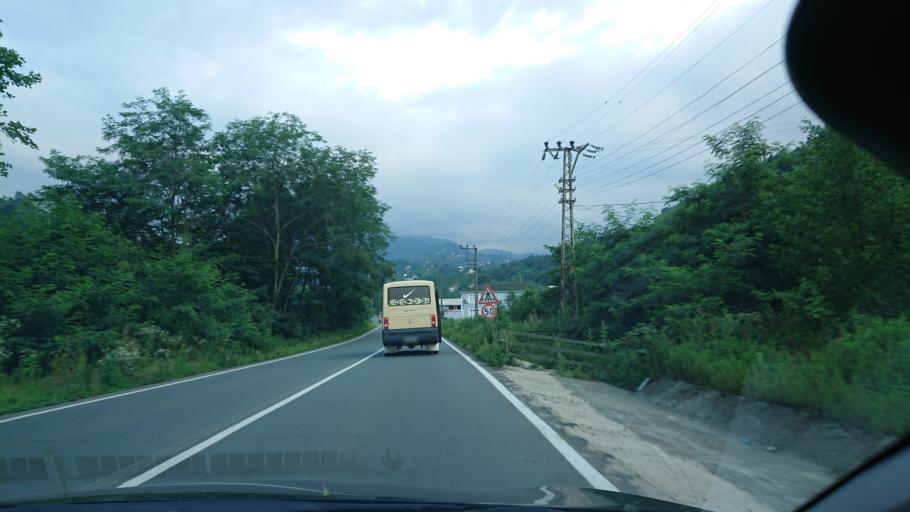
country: TR
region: Rize
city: Cayeli
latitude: 41.0655
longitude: 40.7150
